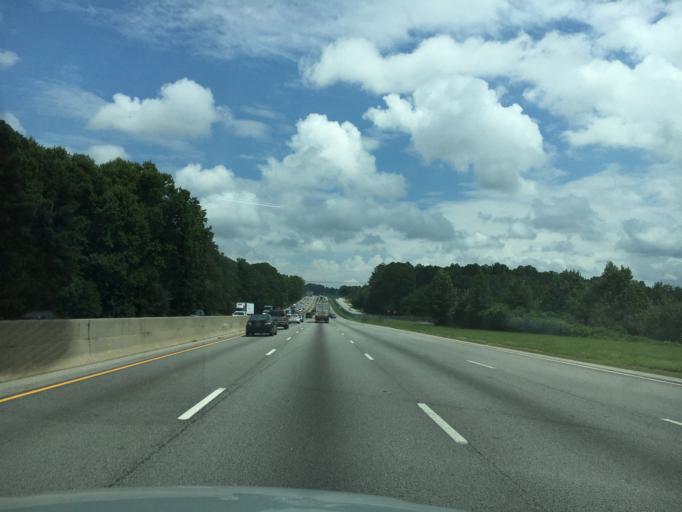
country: US
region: Georgia
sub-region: DeKalb County
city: Lithonia
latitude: 33.6974
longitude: -84.0831
